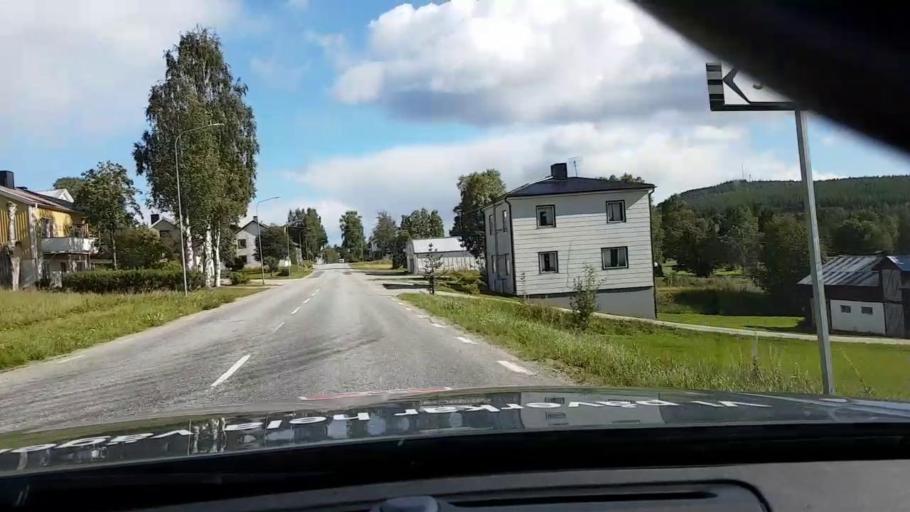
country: SE
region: Vaesterbotten
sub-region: Asele Kommun
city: Asele
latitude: 63.7902
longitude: 17.6338
